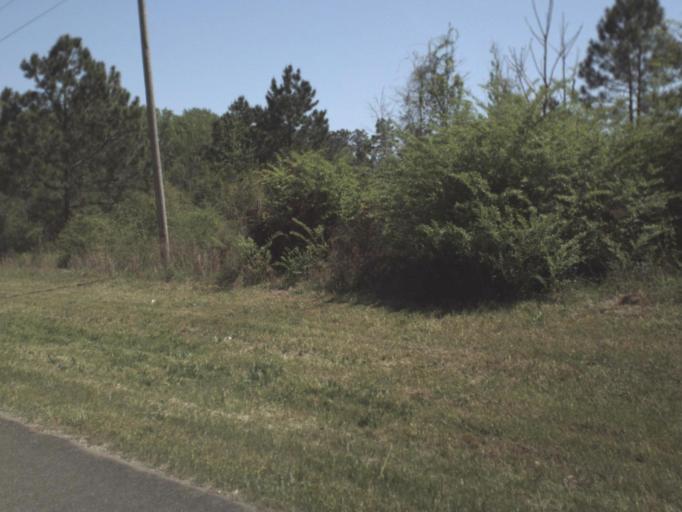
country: US
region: Alabama
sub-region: Escambia County
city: East Brewton
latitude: 30.8994
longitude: -87.0030
